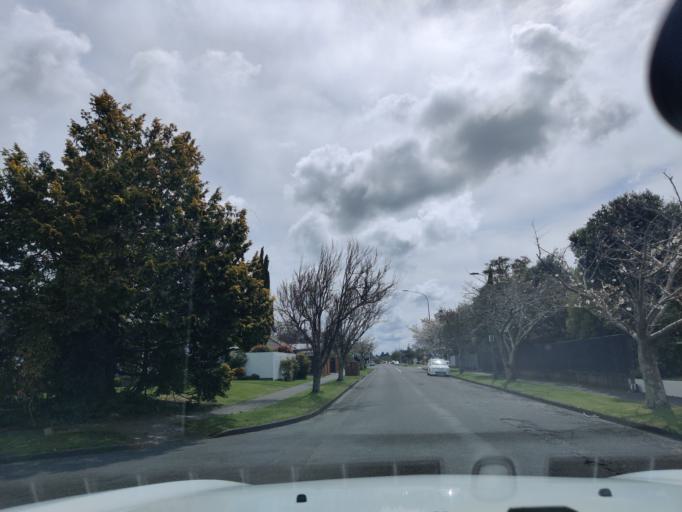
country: NZ
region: Manawatu-Wanganui
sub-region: Palmerston North City
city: Palmerston North
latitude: -40.3786
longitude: 175.5973
